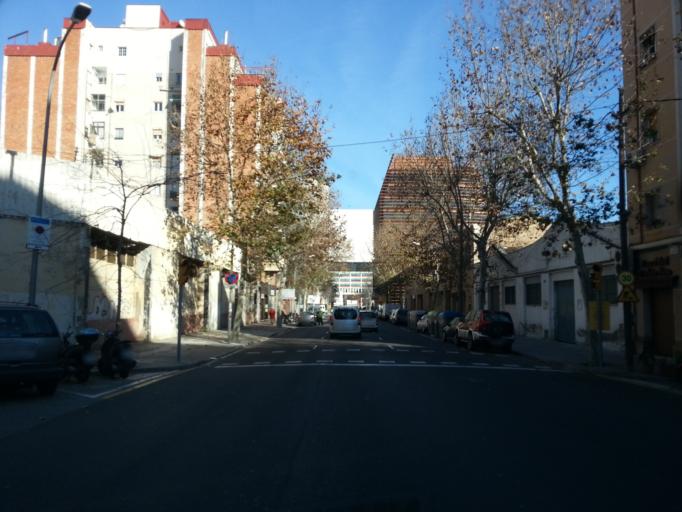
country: ES
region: Catalonia
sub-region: Provincia de Barcelona
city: Sant Marti
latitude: 41.4016
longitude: 2.1893
